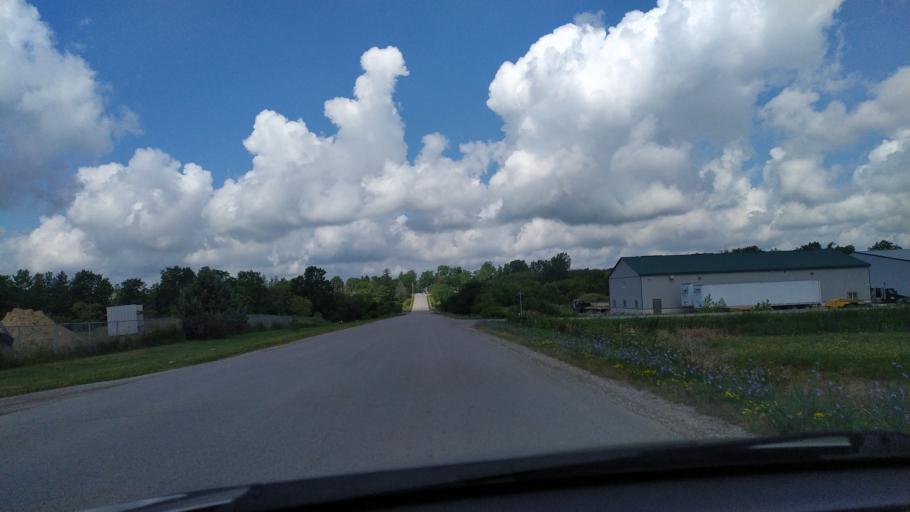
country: CA
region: Ontario
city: Huron East
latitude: 43.4584
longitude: -81.2000
